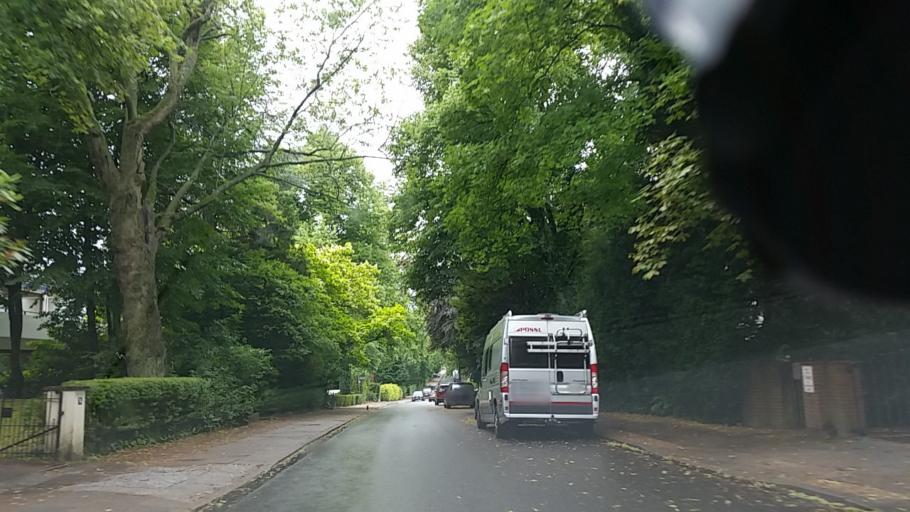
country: DE
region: Hamburg
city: Altona
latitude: 53.5561
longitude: 9.8815
